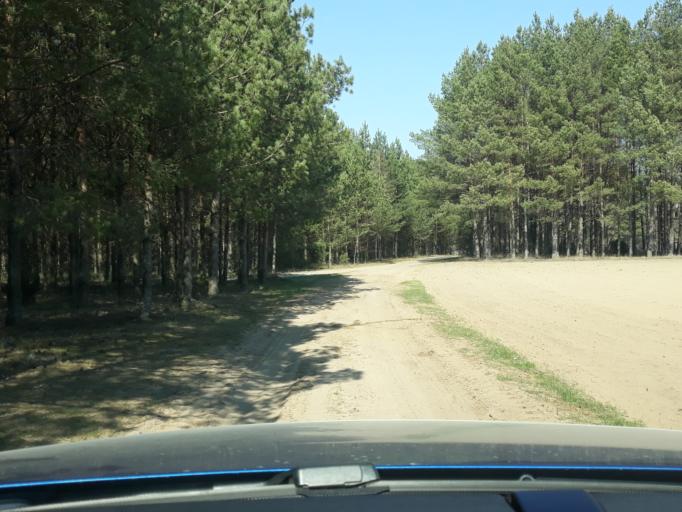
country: PL
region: Pomeranian Voivodeship
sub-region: Powiat bytowski
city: Lipnica
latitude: 53.8615
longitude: 17.4295
